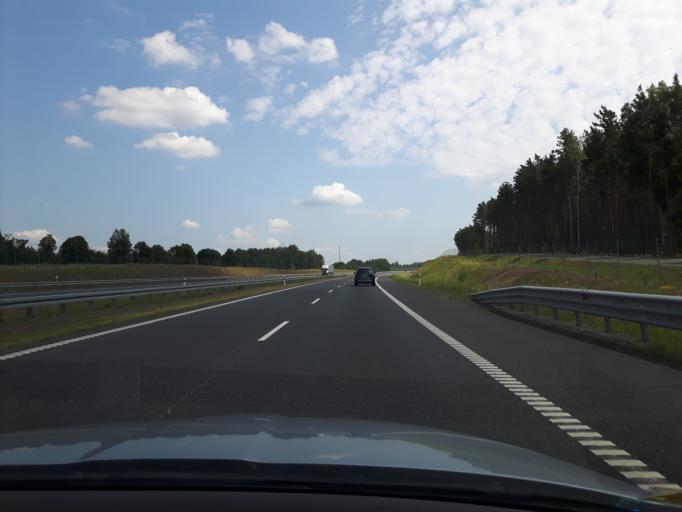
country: PL
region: Warmian-Masurian Voivodeship
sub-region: Powiat olsztynski
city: Olsztynek
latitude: 53.5881
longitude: 20.2335
